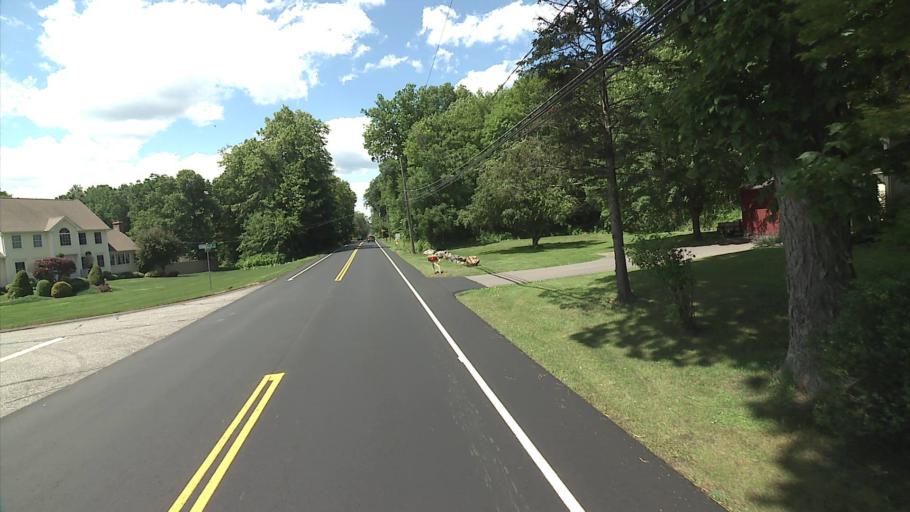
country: US
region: Connecticut
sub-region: Tolland County
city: Somers
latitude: 41.9971
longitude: -72.4311
